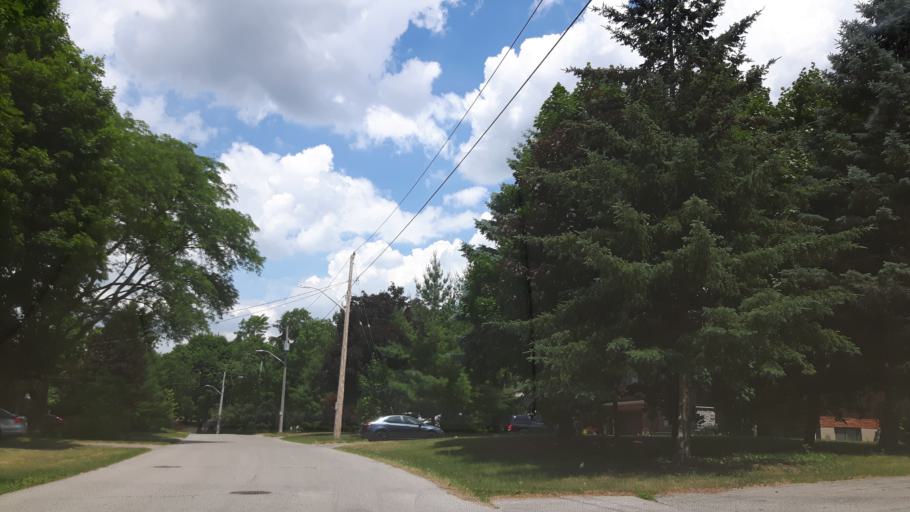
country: CA
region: Ontario
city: London
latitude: 43.0000
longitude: -81.2873
